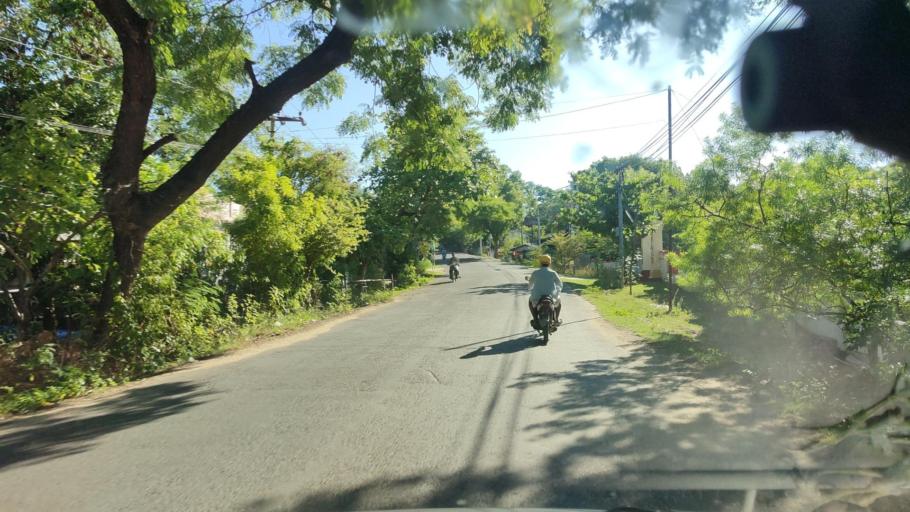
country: MM
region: Magway
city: Yenangyaung
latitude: 20.4704
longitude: 94.8840
